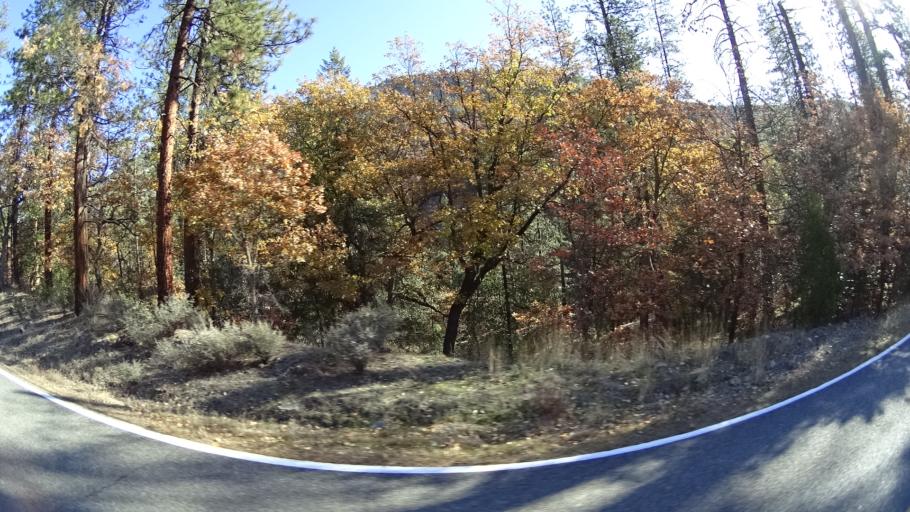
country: US
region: California
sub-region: Siskiyou County
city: Yreka
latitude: 41.8804
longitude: -122.8221
